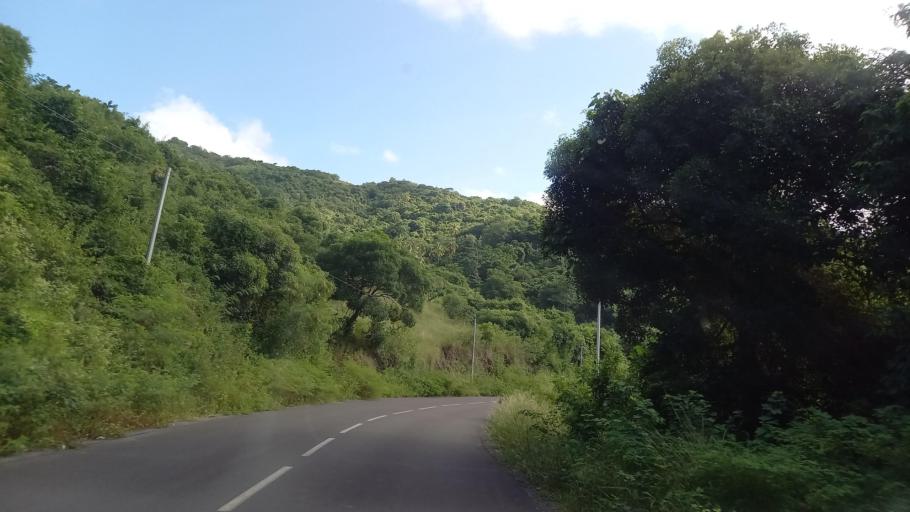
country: YT
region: Kani-Keli
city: Kani Keli
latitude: -12.9872
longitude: 45.1331
